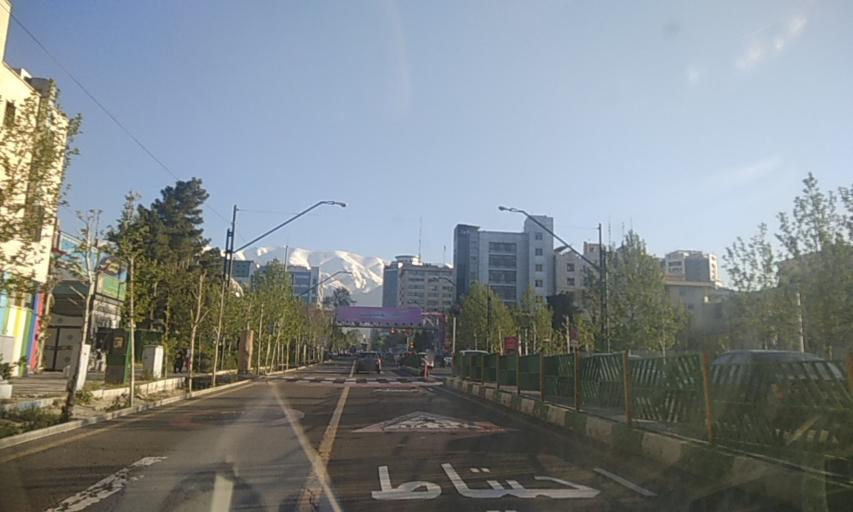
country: IR
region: Tehran
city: Tajrish
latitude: 35.7649
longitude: 51.4106
